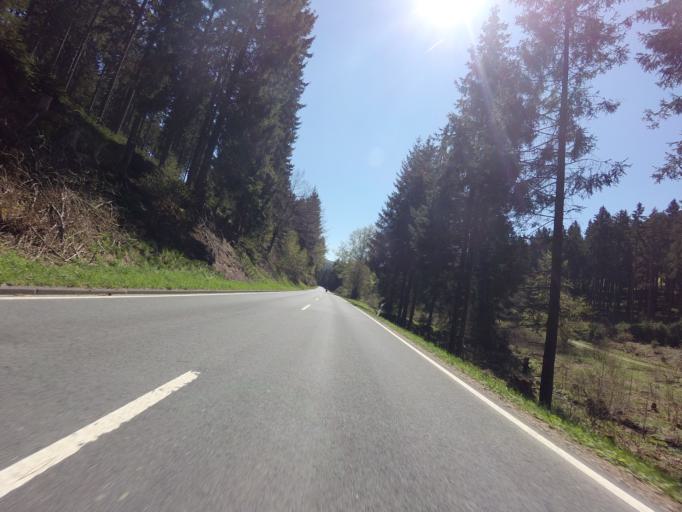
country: DE
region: North Rhine-Westphalia
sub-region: Regierungsbezirk Arnsberg
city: Erndtebruck
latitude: 51.0650
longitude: 8.2195
